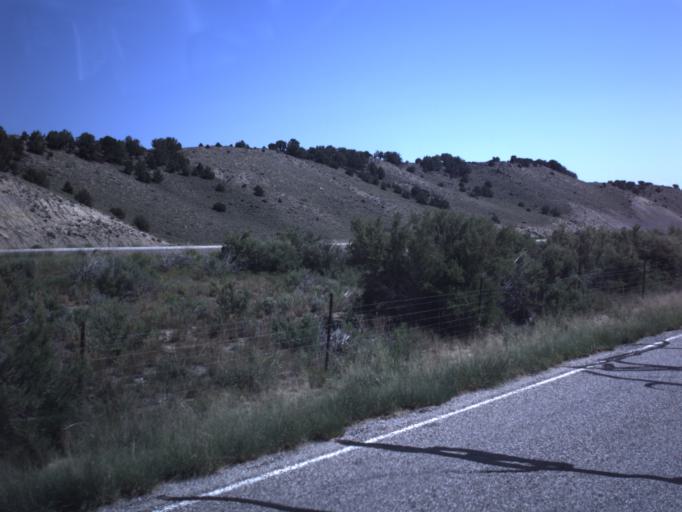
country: US
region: Utah
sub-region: Emery County
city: Ferron
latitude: 38.7591
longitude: -111.3716
